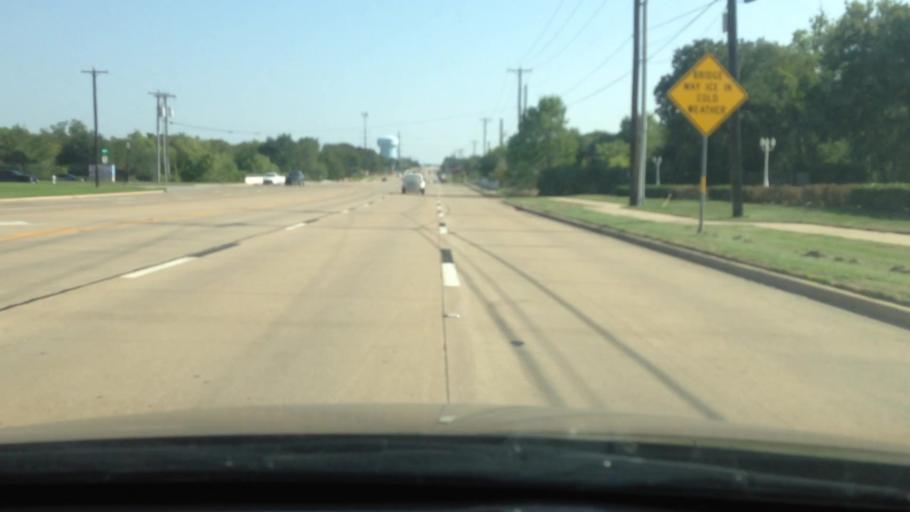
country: US
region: Texas
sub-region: Tarrant County
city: Colleyville
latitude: 32.8855
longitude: -97.1860
